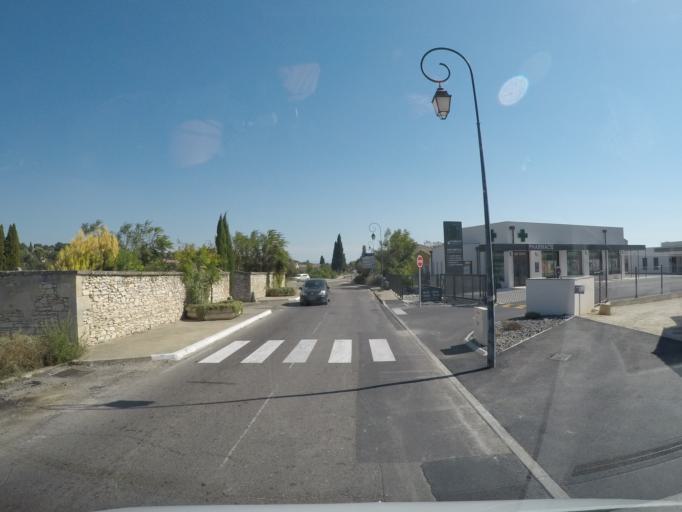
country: FR
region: Languedoc-Roussillon
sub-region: Departement du Gard
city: Tavel
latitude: 44.0108
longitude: 4.7062
